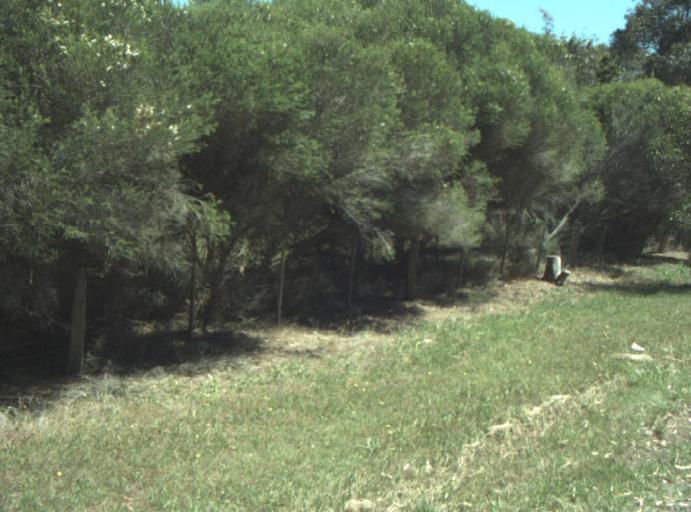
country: AU
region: Victoria
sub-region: Greater Geelong
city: Breakwater
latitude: -38.2524
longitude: 144.3504
